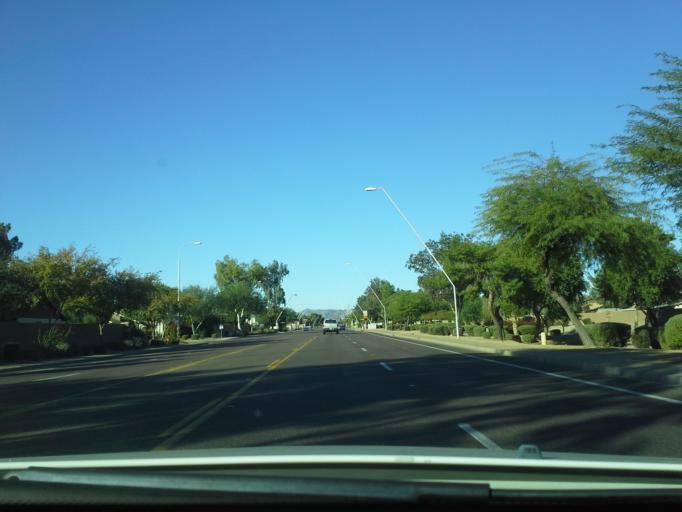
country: US
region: Arizona
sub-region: Maricopa County
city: San Carlos
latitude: 33.3496
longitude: -111.8709
